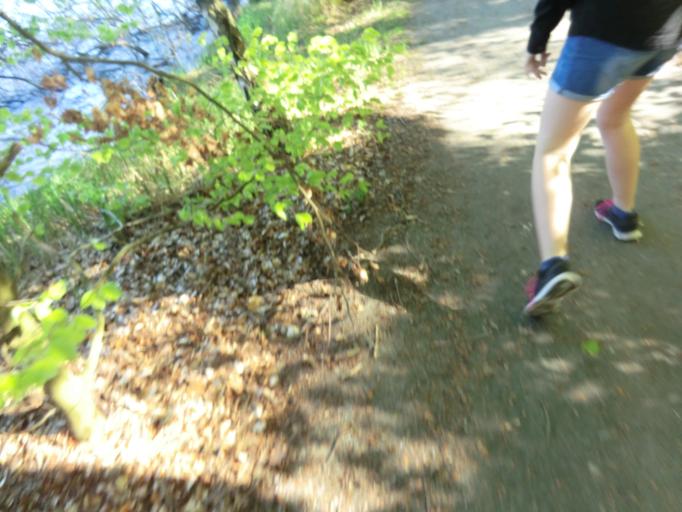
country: SE
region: Skane
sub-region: Sjobo Kommun
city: Sjoebo
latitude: 55.5684
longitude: 13.7190
